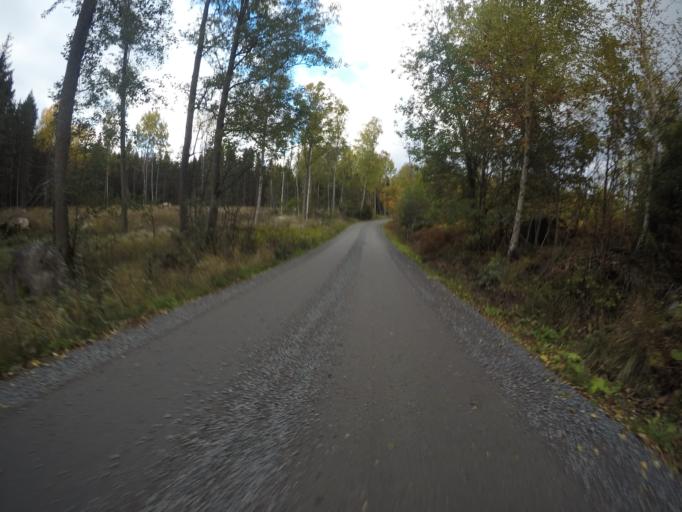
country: SE
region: Vaestmanland
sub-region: Arboga Kommun
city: Tyringe
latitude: 59.3052
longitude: 15.9785
